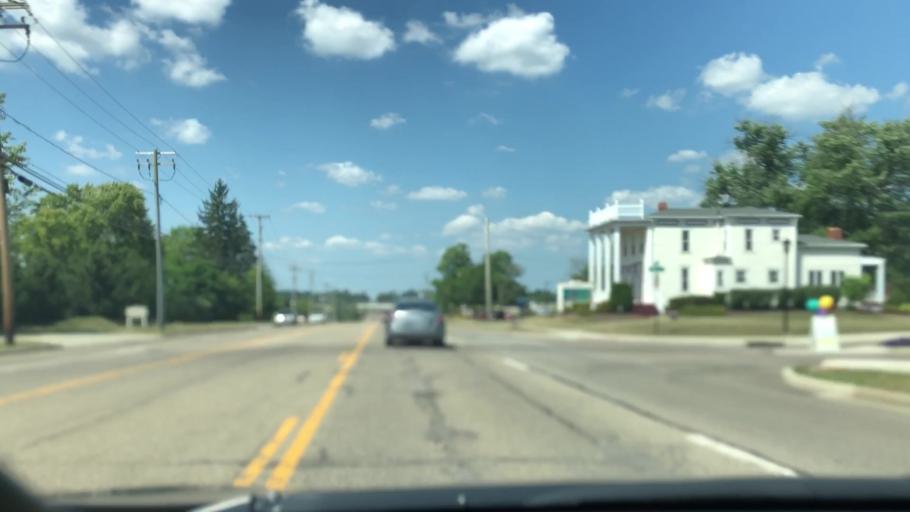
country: US
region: Ohio
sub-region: Summit County
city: Green
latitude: 40.9528
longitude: -81.4658
